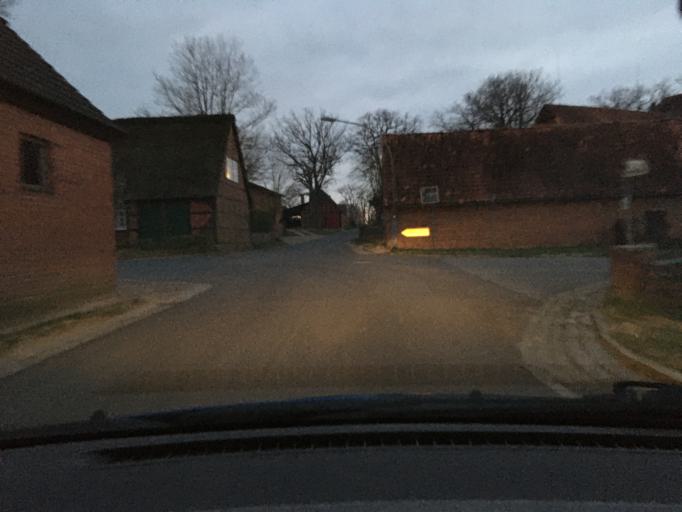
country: DE
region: Lower Saxony
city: Thomasburg
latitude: 53.2240
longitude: 10.6298
